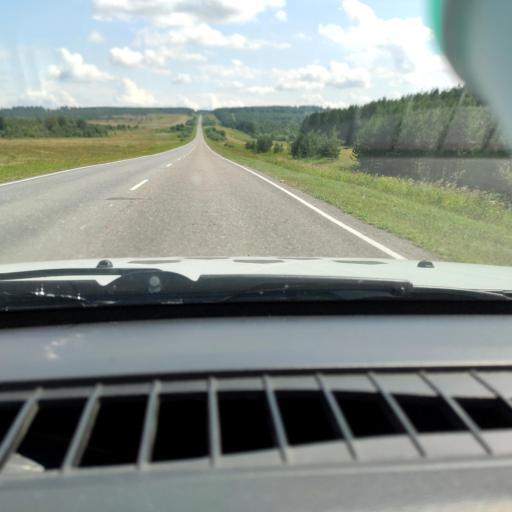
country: RU
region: Chelyabinsk
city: Mezhevoy
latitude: 55.3049
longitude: 58.7422
